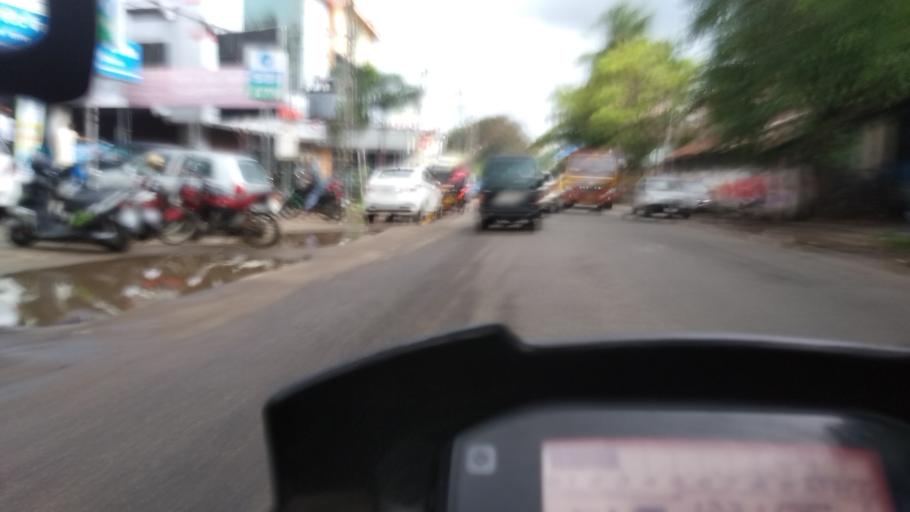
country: IN
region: Kerala
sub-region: Thiruvananthapuram
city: Attingal
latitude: 8.7049
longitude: 76.8149
